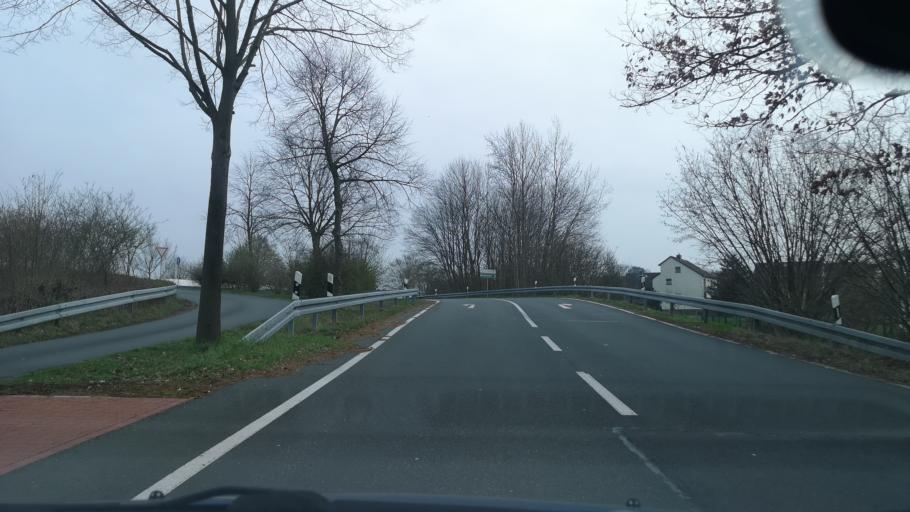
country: DE
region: Lower Saxony
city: Garbsen
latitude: 52.4636
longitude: 9.5318
